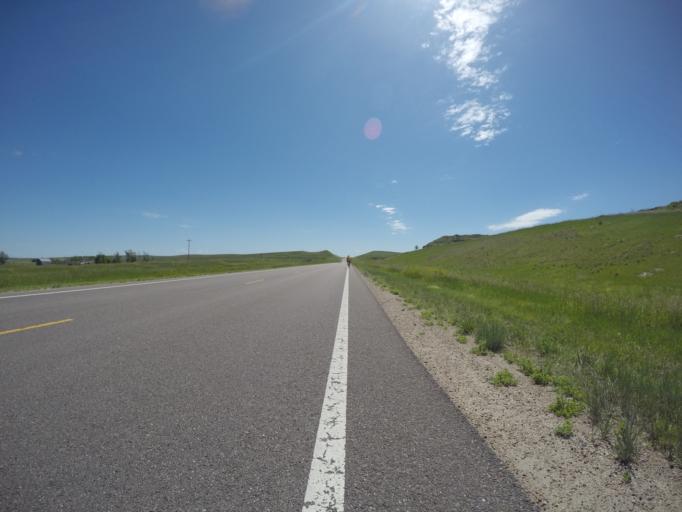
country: US
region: Kansas
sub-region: Rawlins County
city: Atwood
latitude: 39.8134
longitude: -101.0062
